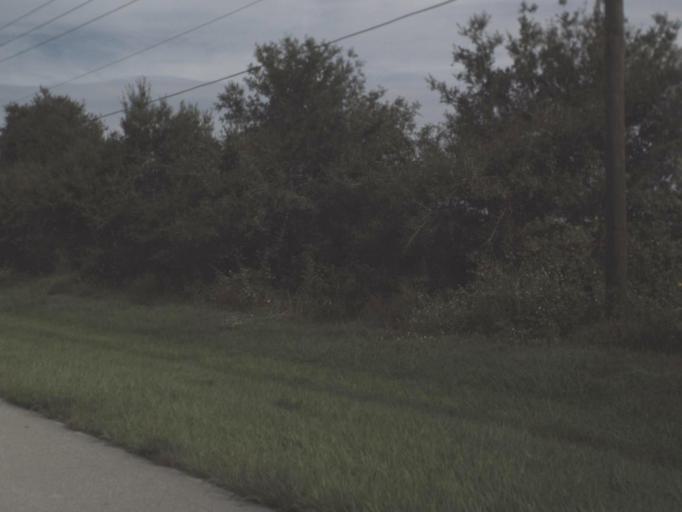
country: US
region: Florida
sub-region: DeSoto County
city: Southeast Arcadia
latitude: 27.1671
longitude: -81.8227
